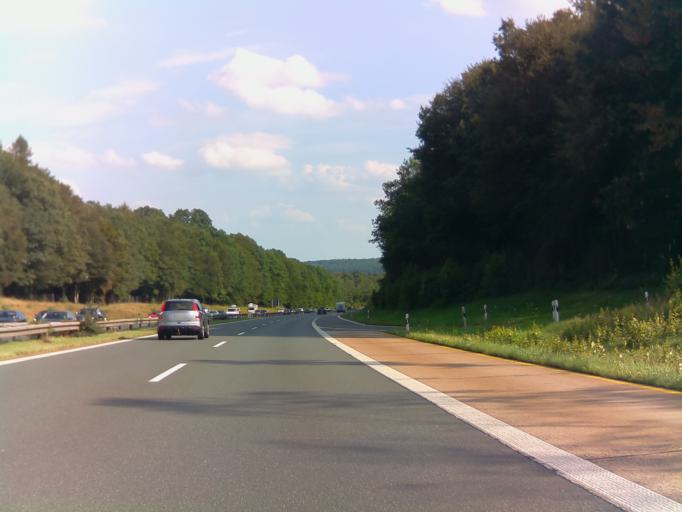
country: DE
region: Bavaria
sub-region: Regierungsbezirk Unterfranken
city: Oberthulba
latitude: 50.2075
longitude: 9.9303
